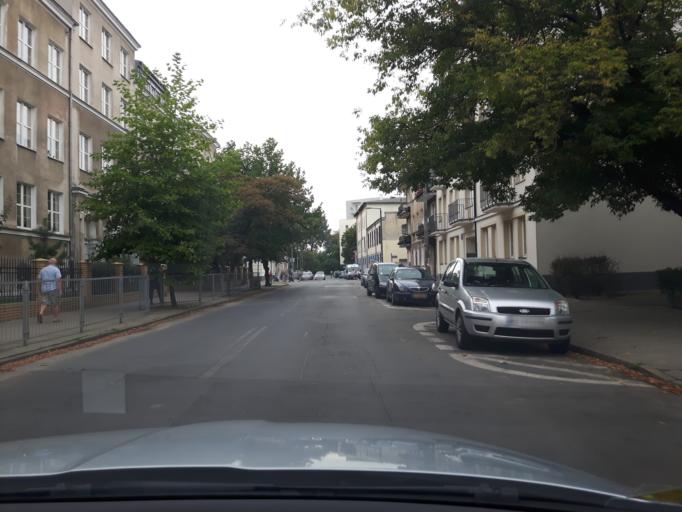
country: PL
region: Masovian Voivodeship
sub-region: Warszawa
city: Praga Polnoc
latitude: 52.2595
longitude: 21.0578
